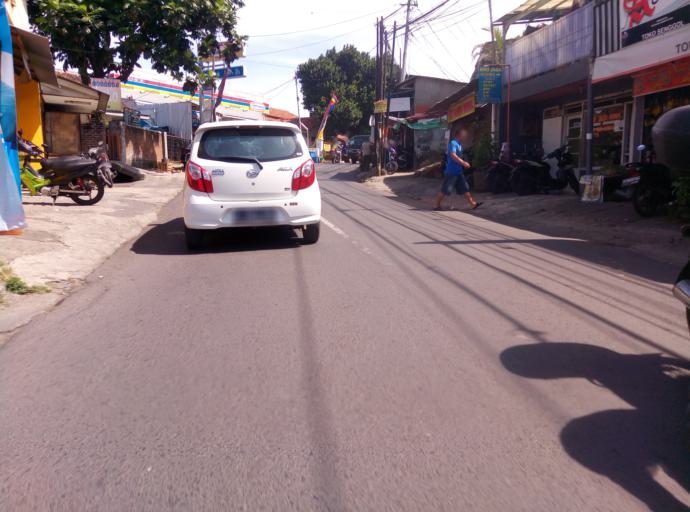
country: ID
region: West Java
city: Bandung
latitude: -6.8921
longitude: 107.6289
